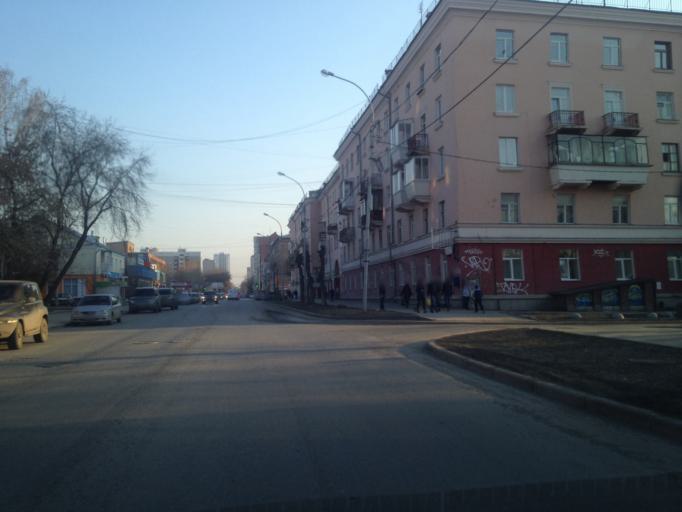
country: RU
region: Sverdlovsk
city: Yekaterinburg
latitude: 56.8349
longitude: 60.5528
